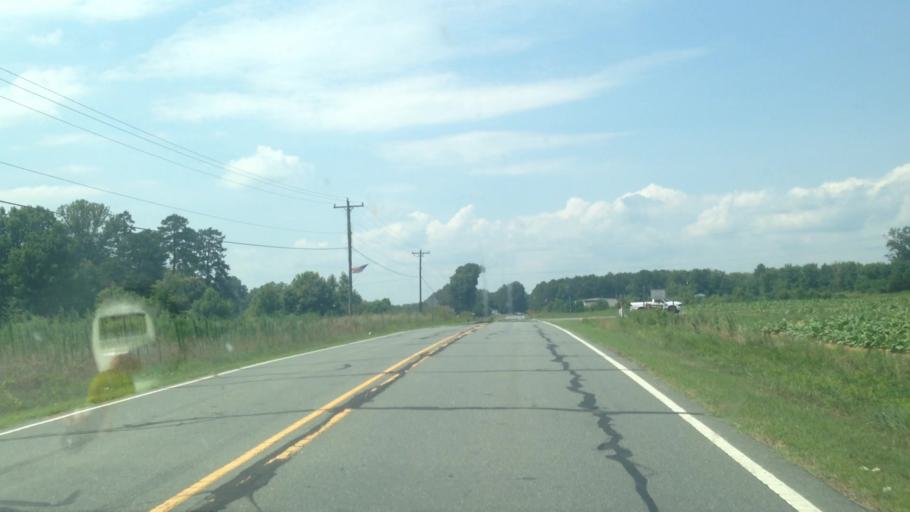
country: US
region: North Carolina
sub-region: Stokes County
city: Walnut Cove
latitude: 36.3357
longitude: -80.0497
